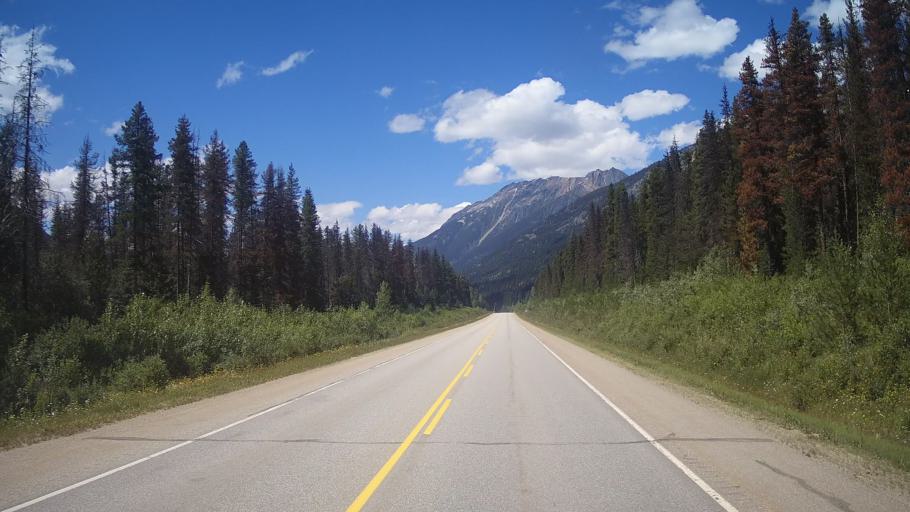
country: CA
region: Alberta
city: Grande Cache
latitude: 52.9928
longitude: -119.0160
